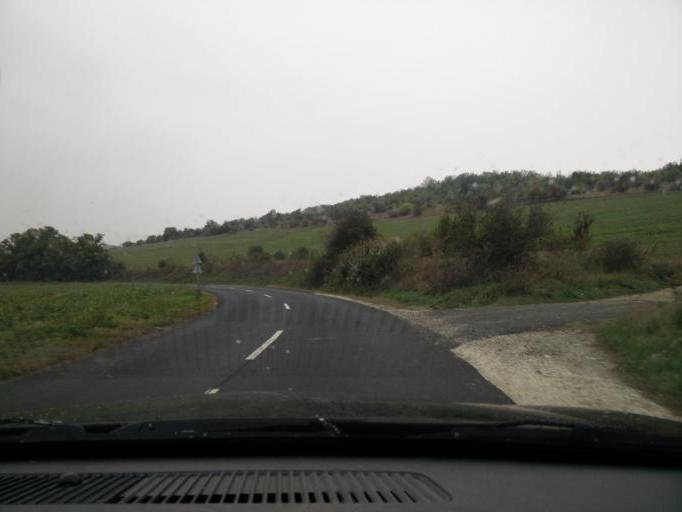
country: HU
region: Komarom-Esztergom
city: Piliscsev
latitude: 47.6483
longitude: 18.7817
